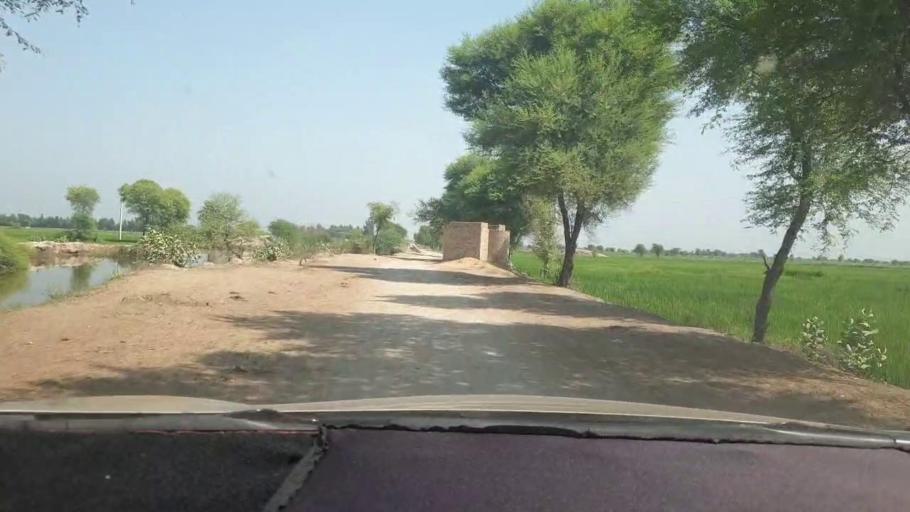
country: PK
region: Sindh
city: Miro Khan
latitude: 27.6752
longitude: 68.1350
